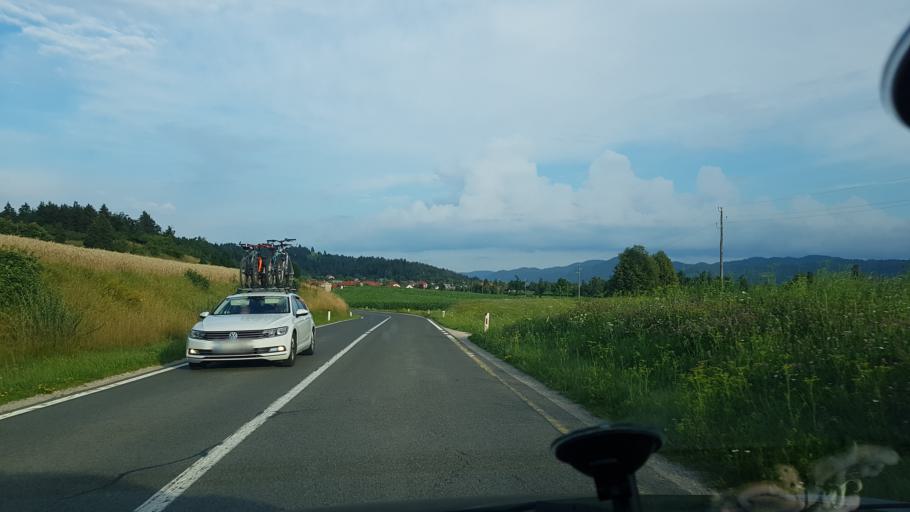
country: SI
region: Logatec
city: Logatec
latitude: 45.9341
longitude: 14.1314
